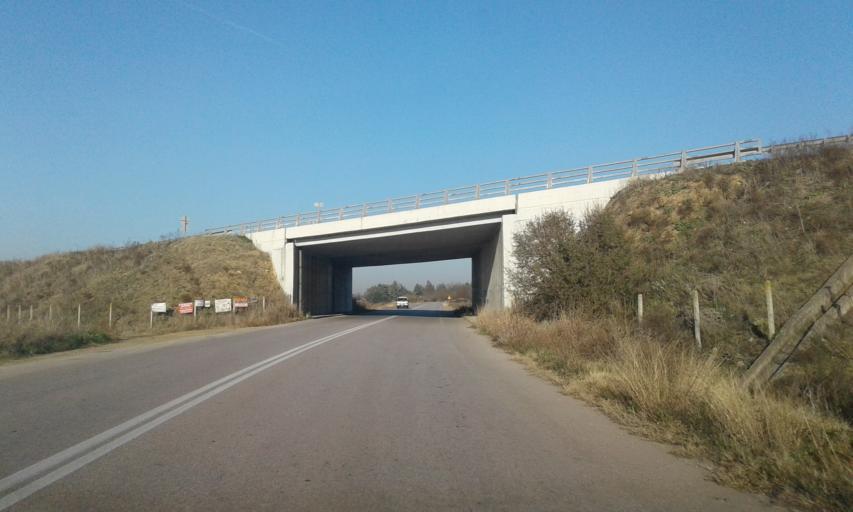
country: GR
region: Central Macedonia
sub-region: Nomos Thessalonikis
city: Kolchikon
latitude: 40.7091
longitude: 23.1822
